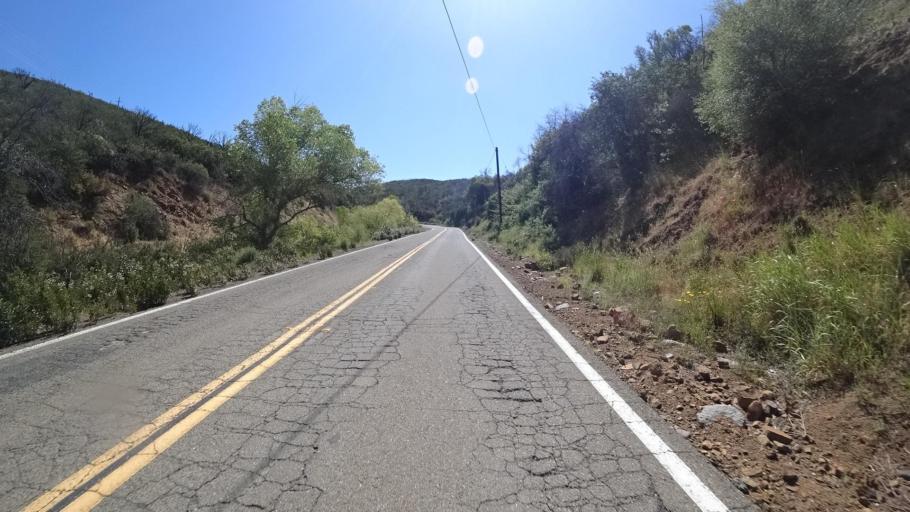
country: US
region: California
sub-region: Lake County
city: Hidden Valley Lake
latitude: 38.8866
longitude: -122.5026
